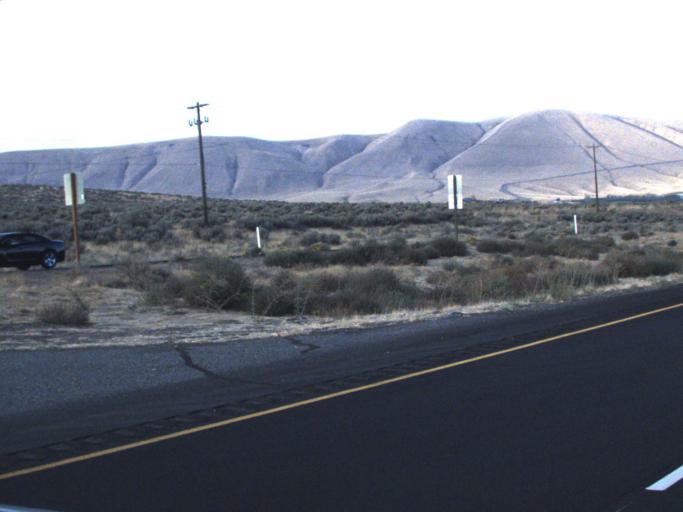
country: US
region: Washington
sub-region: Benton County
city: Benton City
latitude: 46.2558
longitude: -119.4552
